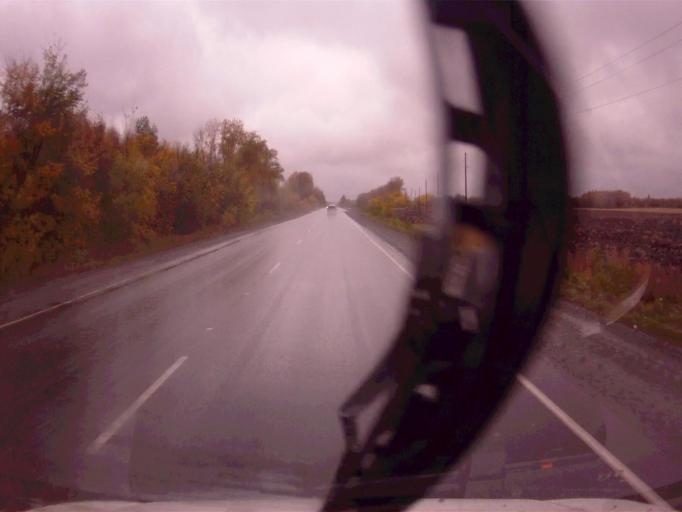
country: RU
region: Chelyabinsk
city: Argayash
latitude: 55.4324
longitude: 60.9854
